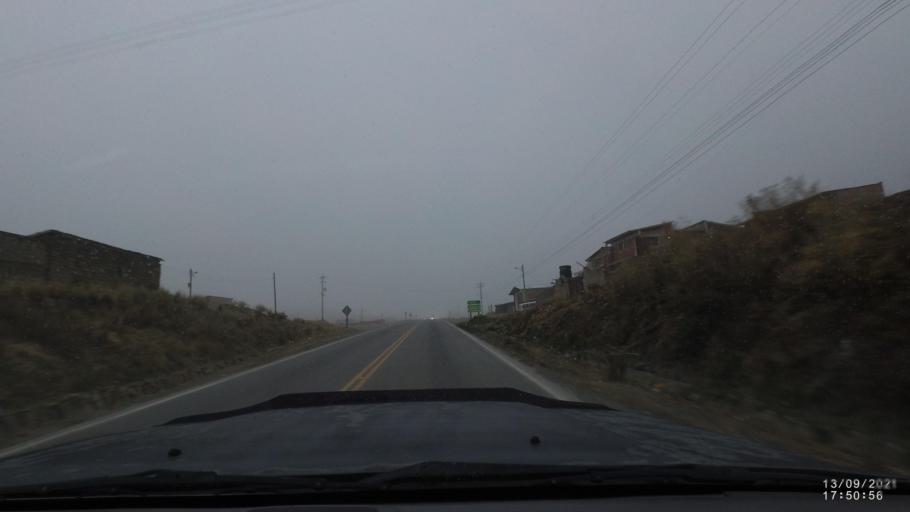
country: BO
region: Cochabamba
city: Colomi
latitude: -17.3969
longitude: -65.8647
